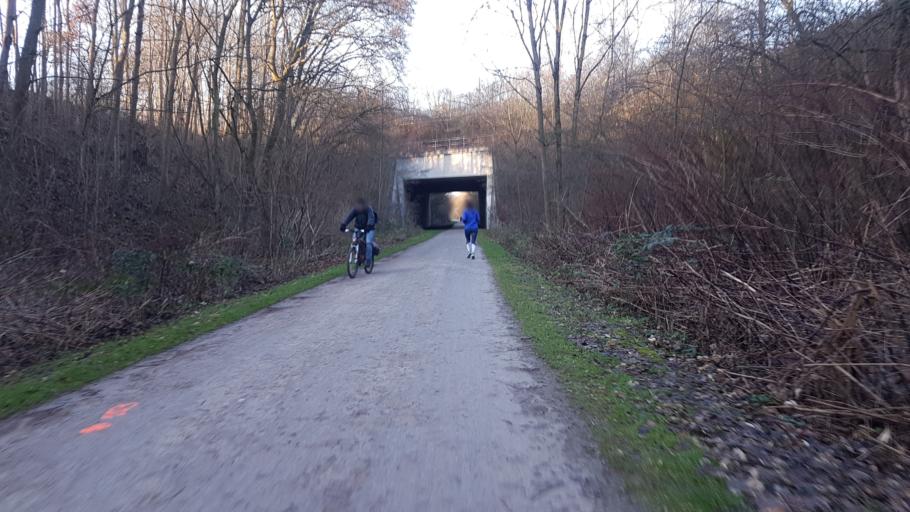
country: DE
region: North Rhine-Westphalia
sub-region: Regierungsbezirk Dusseldorf
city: Essen
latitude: 51.4395
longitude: 6.9589
